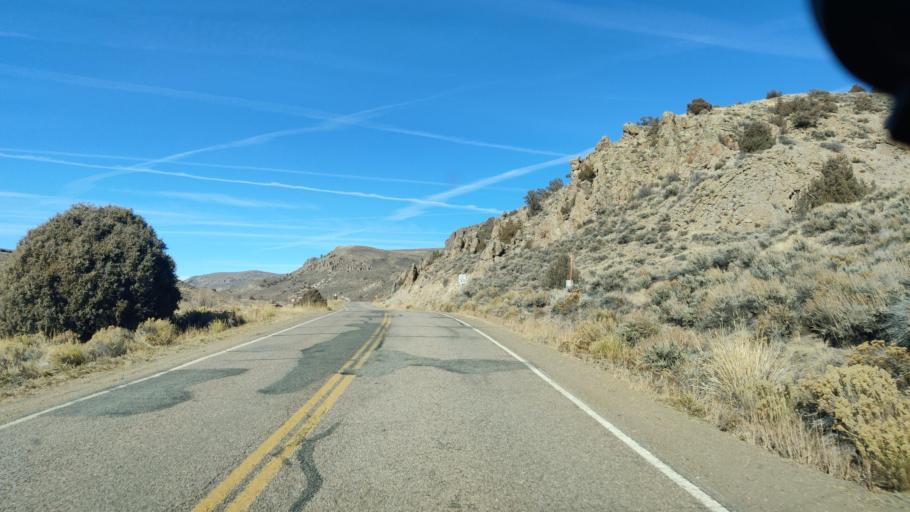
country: US
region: Colorado
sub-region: Gunnison County
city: Gunnison
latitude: 38.5736
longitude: -106.9611
